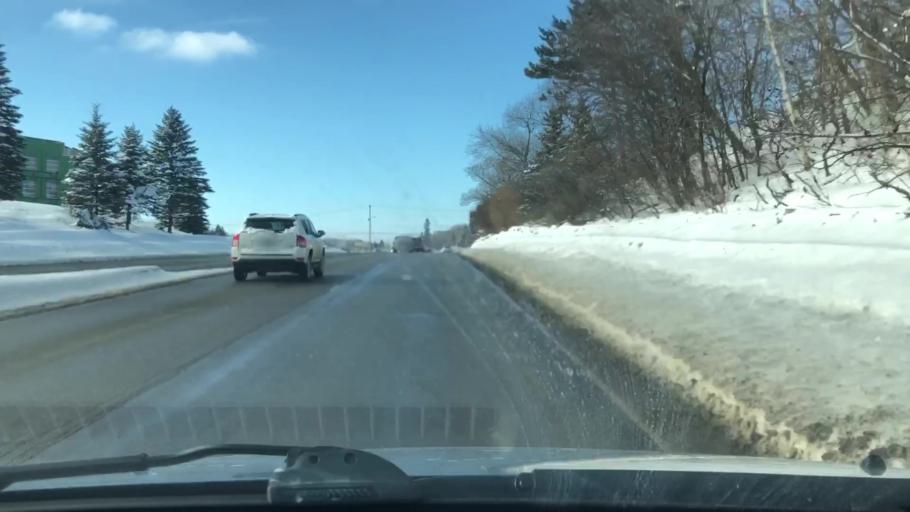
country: US
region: Minnesota
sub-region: Saint Louis County
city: Duluth
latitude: 46.7999
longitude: -92.1189
